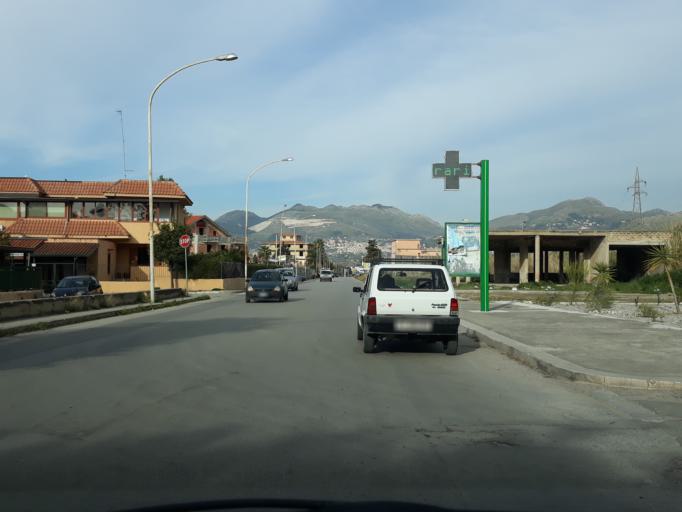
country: IT
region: Sicily
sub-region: Palermo
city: Partinico
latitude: 38.0523
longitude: 13.1260
